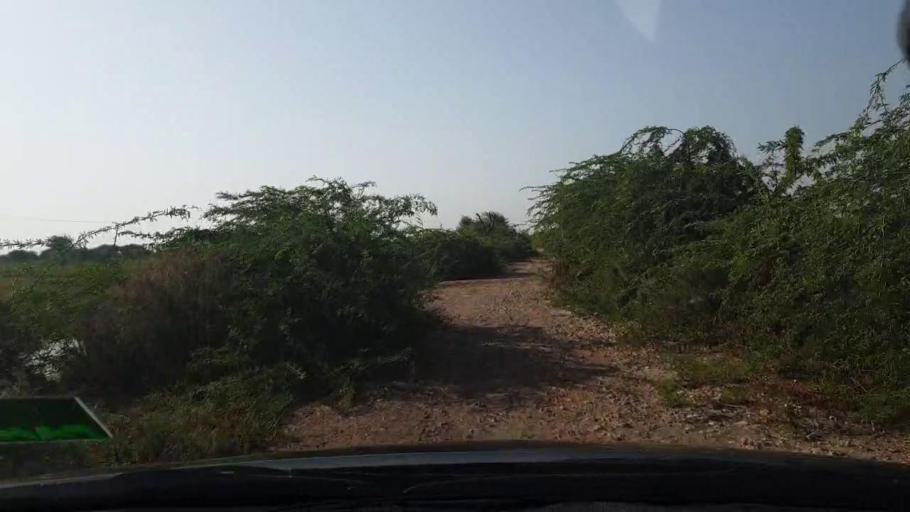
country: PK
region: Sindh
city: Tando Bago
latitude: 24.7083
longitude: 68.9550
